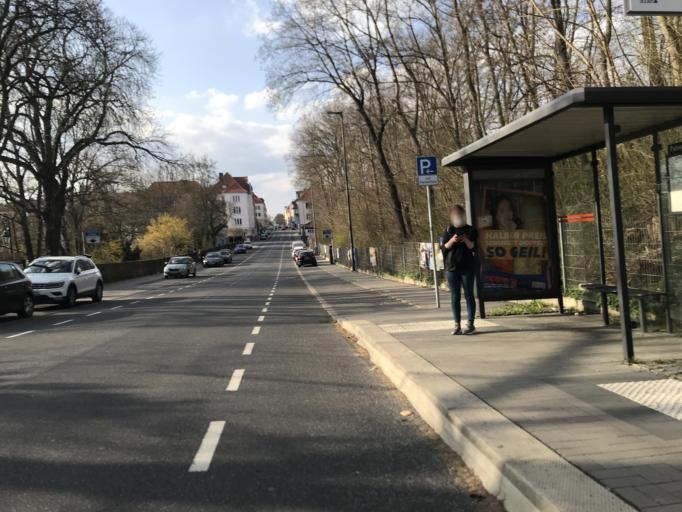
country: DE
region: Hesse
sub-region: Regierungsbezirk Kassel
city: Fulda
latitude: 50.5566
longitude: 9.6806
